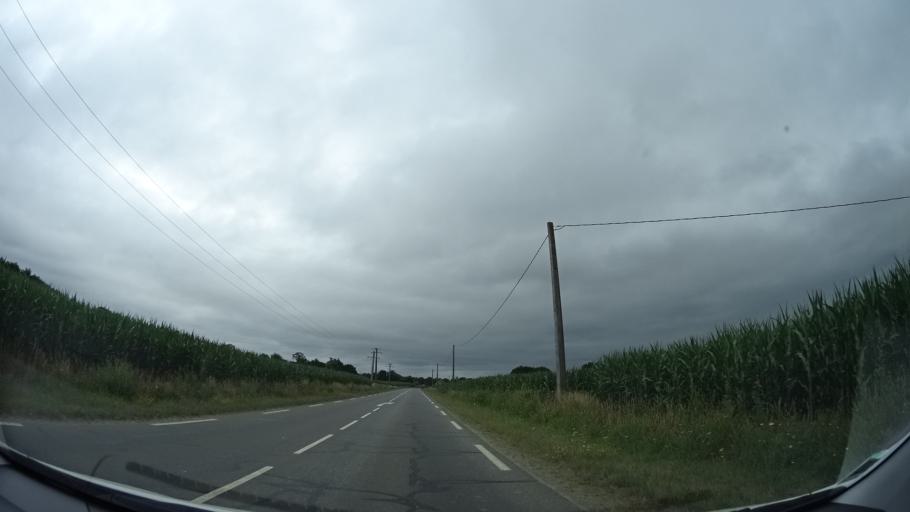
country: FR
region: Brittany
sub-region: Departement d'Ille-et-Vilaine
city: Combourg
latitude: 48.4016
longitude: -1.7458
